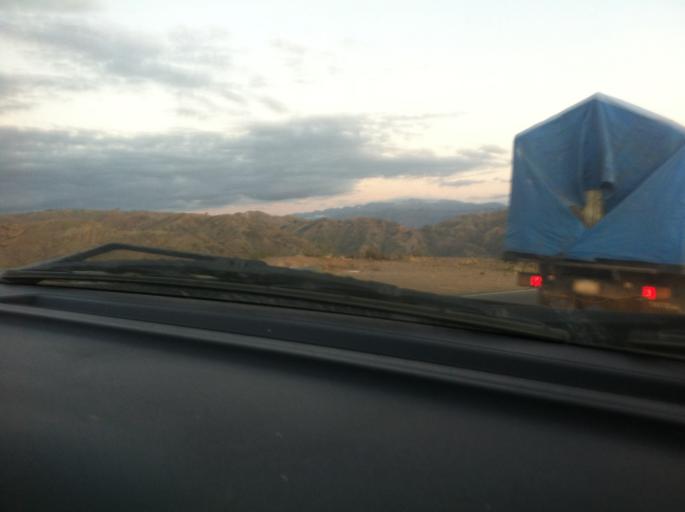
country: BO
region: Cochabamba
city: Irpa Irpa
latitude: -17.6457
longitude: -66.3933
